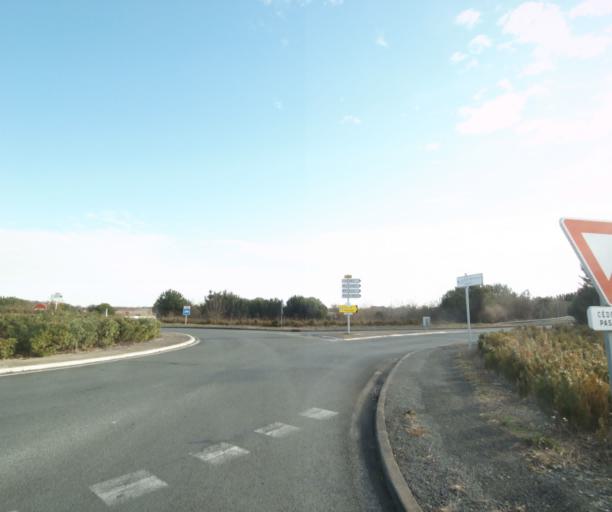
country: FR
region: Poitou-Charentes
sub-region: Departement de la Charente-Maritime
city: Saint-Romain-de-Benet
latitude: 45.6899
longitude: -0.8360
